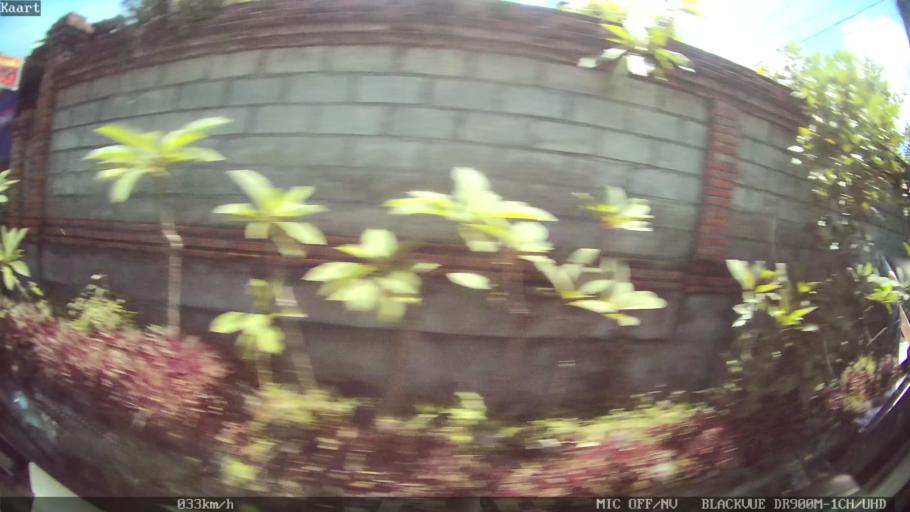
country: ID
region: Bali
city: Banjar Kelodan
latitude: -8.5502
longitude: 115.3351
